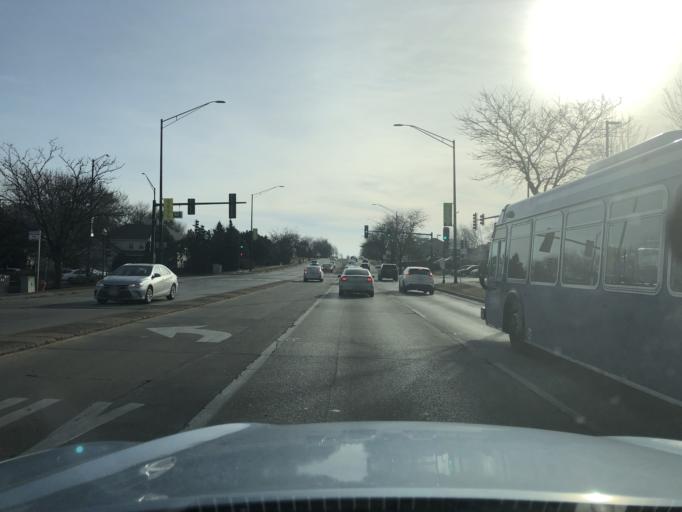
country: US
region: Illinois
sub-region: DuPage County
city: Roselle
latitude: 42.0060
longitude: -88.0801
